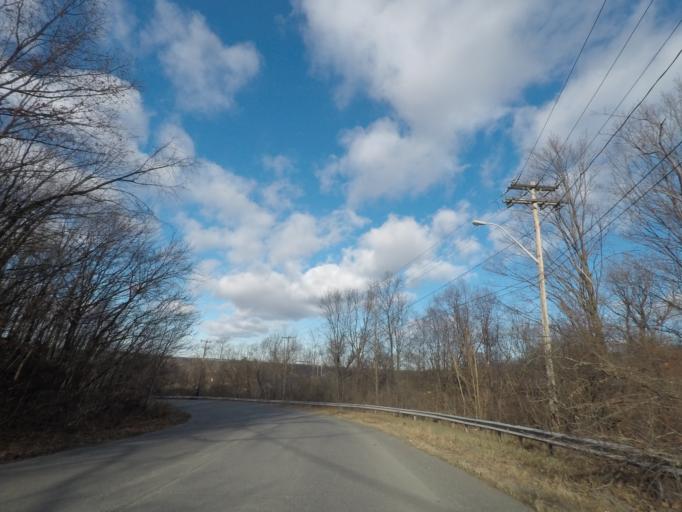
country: US
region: New York
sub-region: Saratoga County
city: Waterford
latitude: 42.7868
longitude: -73.6578
